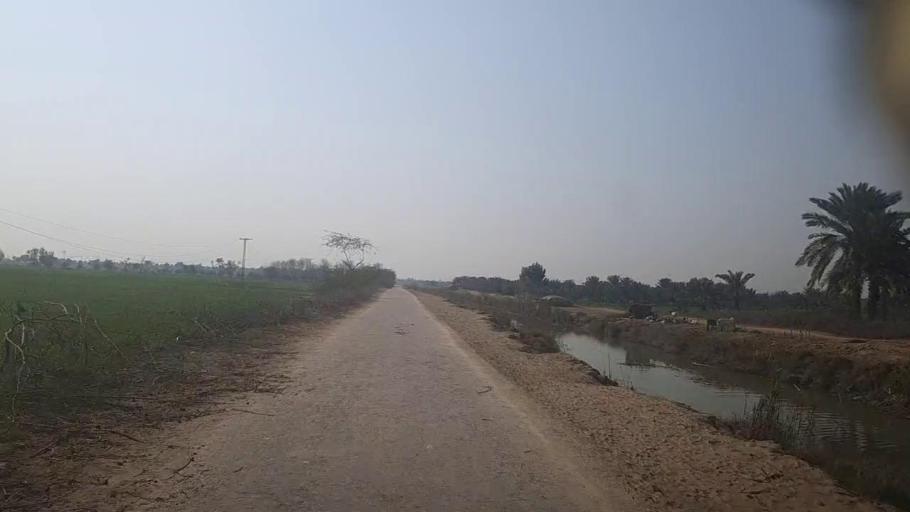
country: PK
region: Sindh
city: Kot Diji
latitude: 27.4085
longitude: 68.7871
